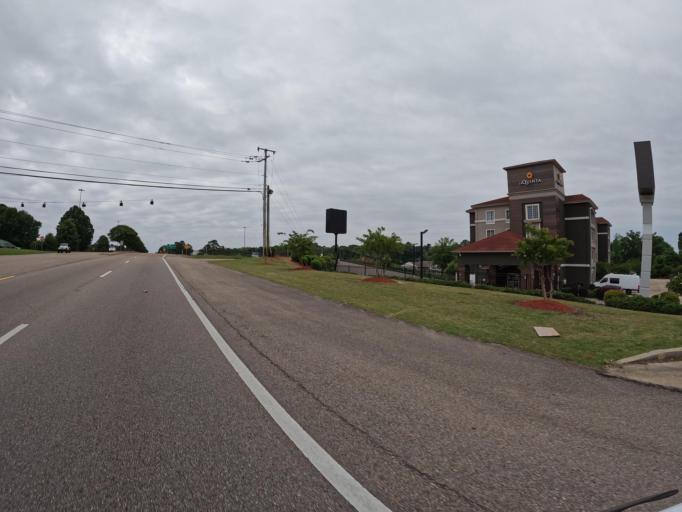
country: US
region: Mississippi
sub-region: Lee County
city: Tupelo
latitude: 34.2771
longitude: -88.7156
